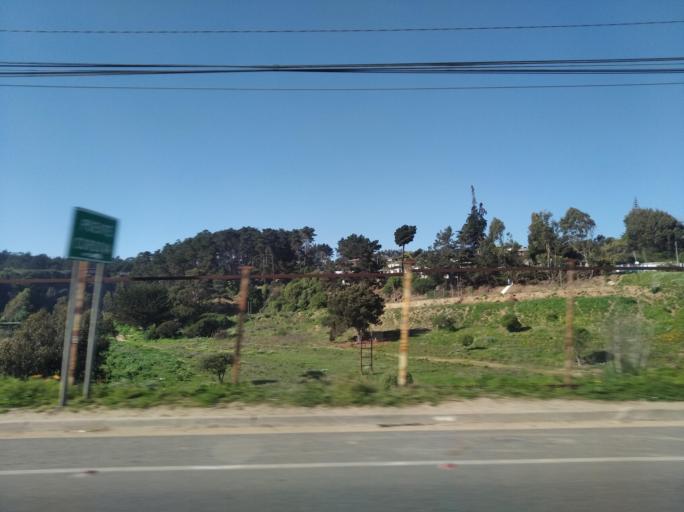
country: CL
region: Valparaiso
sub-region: San Antonio Province
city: El Tabo
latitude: -33.4459
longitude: -71.6783
